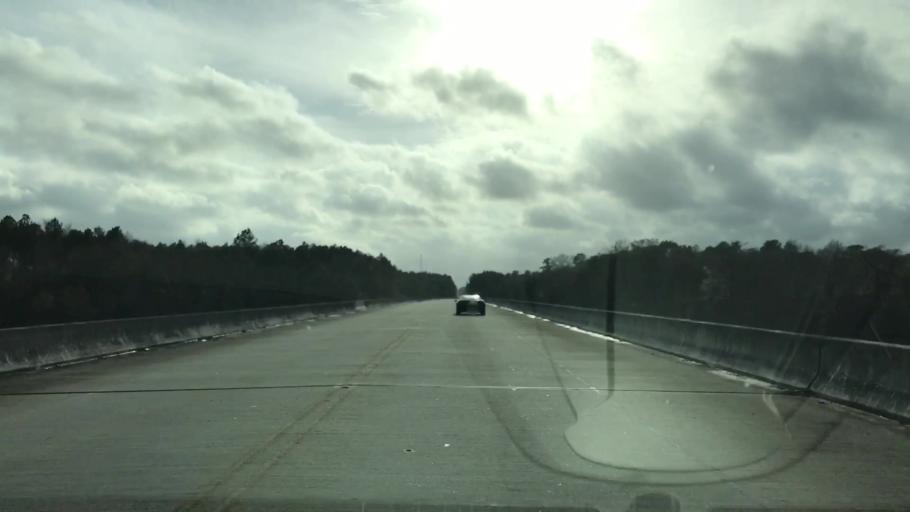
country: US
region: South Carolina
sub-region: Williamsburg County
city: Andrews
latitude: 33.3056
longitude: -79.6774
